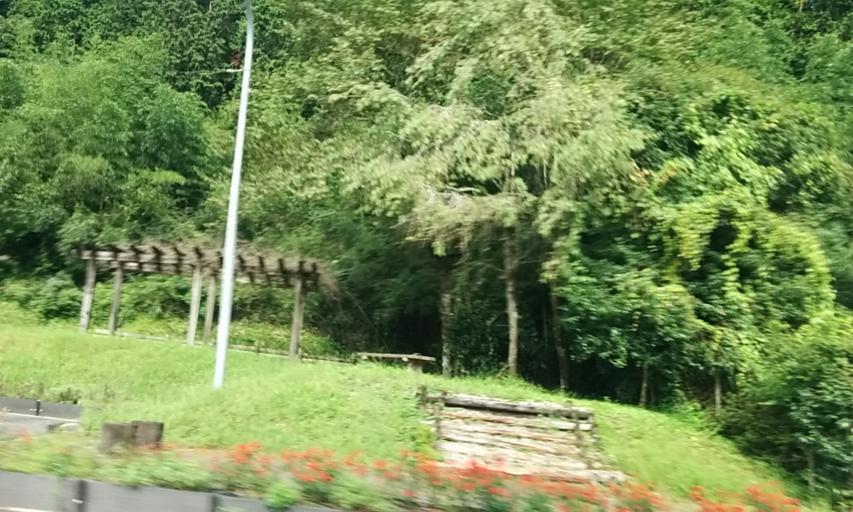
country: JP
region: Gifu
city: Minokamo
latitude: 35.5863
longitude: 137.0848
